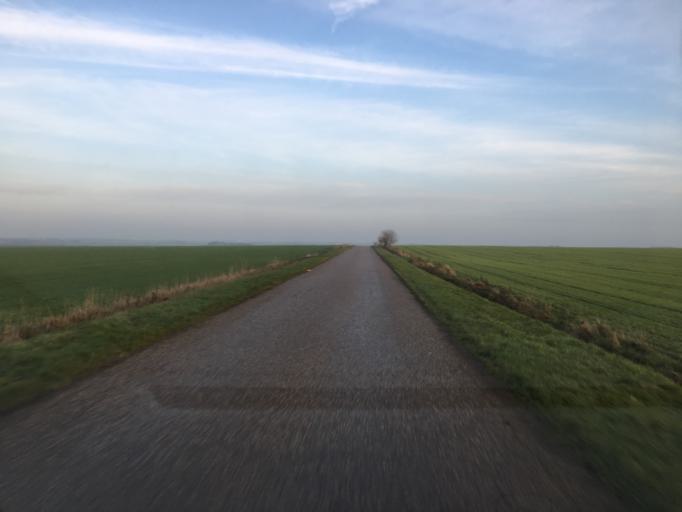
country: DK
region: South Denmark
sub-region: Tonder Kommune
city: Toftlund
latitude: 55.1493
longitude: 9.0920
